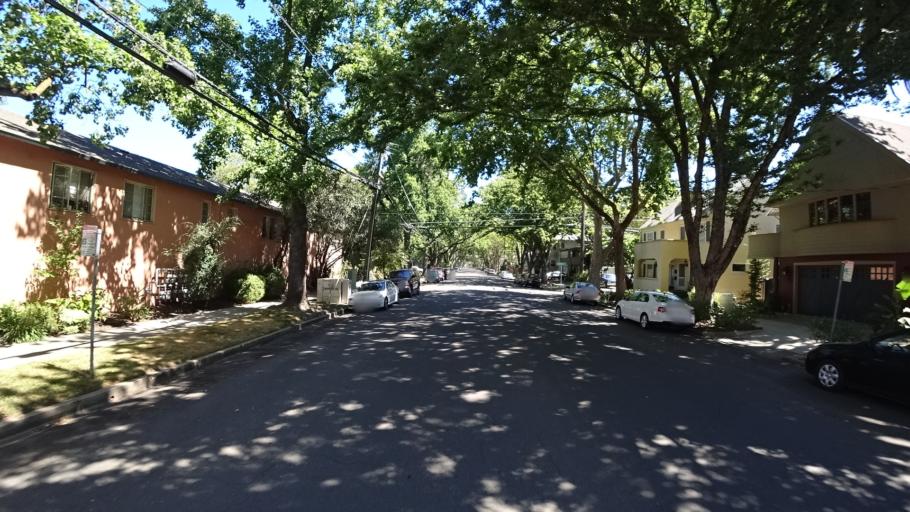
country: US
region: California
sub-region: Sacramento County
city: Sacramento
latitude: 38.5778
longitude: -121.4735
